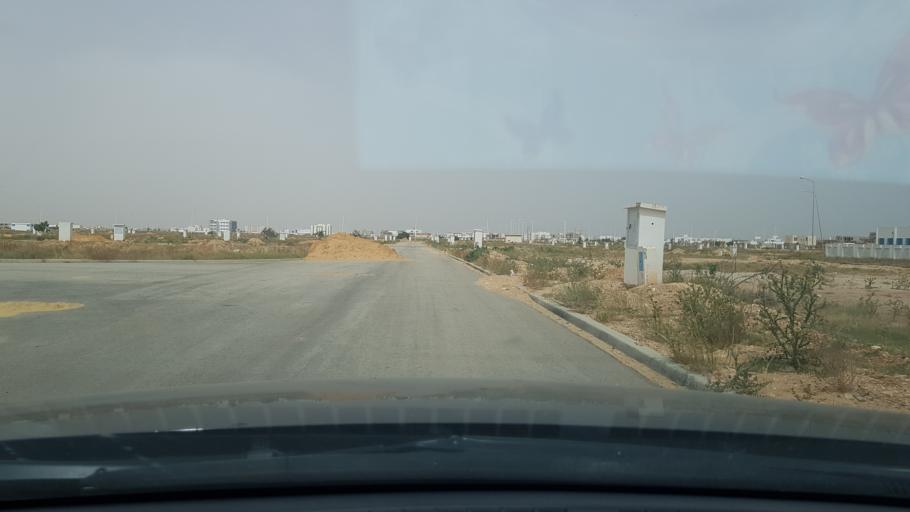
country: TN
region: Safaqis
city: Al Qarmadah
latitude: 34.8262
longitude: 10.7421
